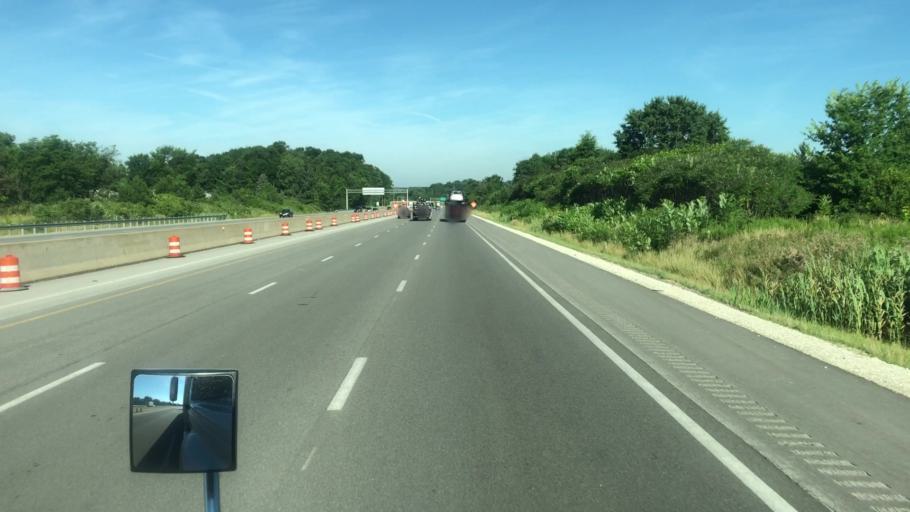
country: US
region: Ohio
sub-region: Portage County
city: Streetsboro
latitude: 41.2542
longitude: -81.3506
